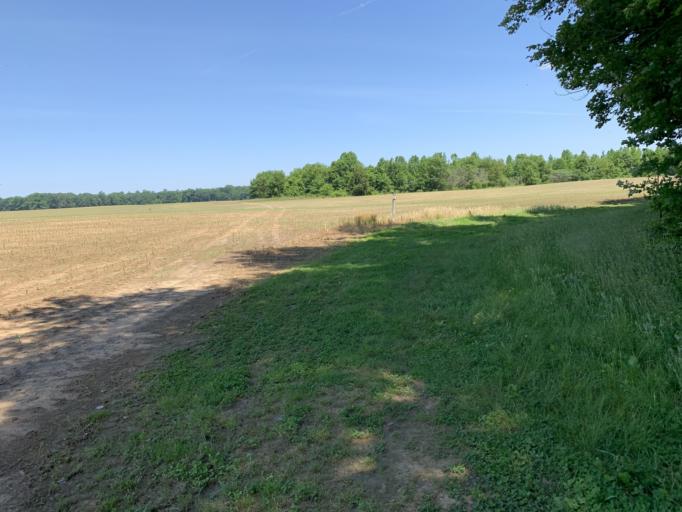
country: US
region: Delaware
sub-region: Kent County
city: Clayton
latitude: 39.3300
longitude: -75.6727
